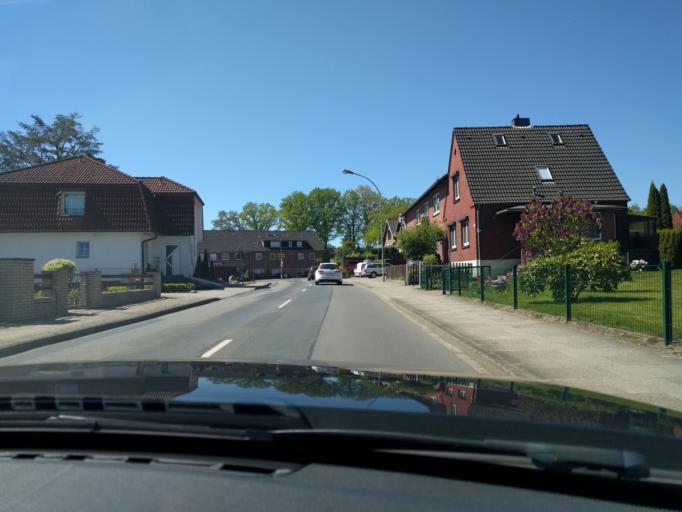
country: DE
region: Lower Saxony
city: Seevetal
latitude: 53.4063
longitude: 10.0018
